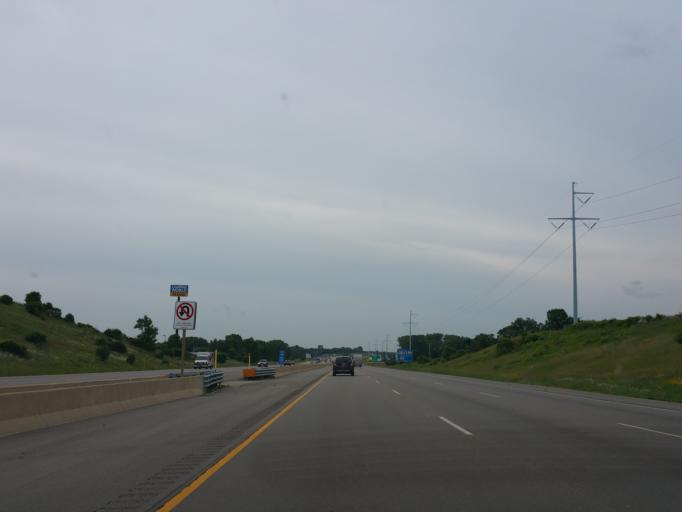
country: US
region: Wisconsin
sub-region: Dane County
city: Windsor
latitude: 43.1856
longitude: -89.3335
